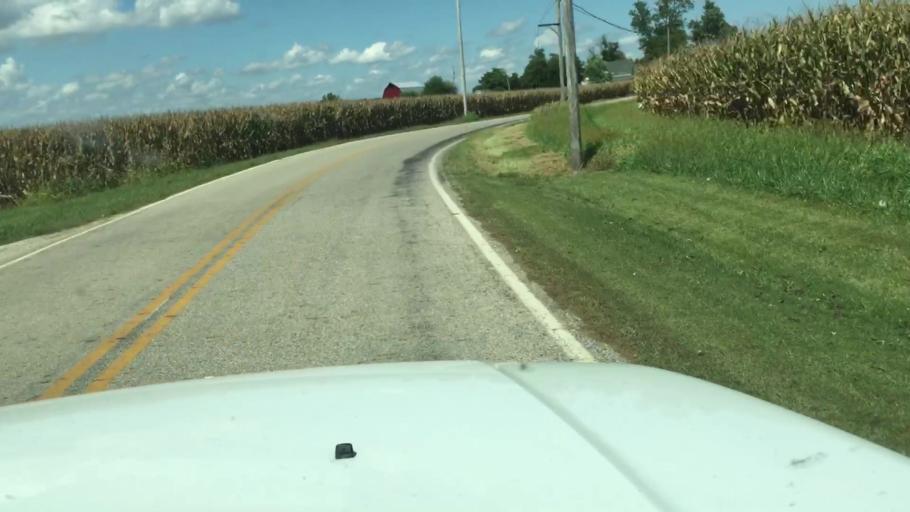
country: US
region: Ohio
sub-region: Madison County
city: Mount Sterling
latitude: 39.6802
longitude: -83.2359
